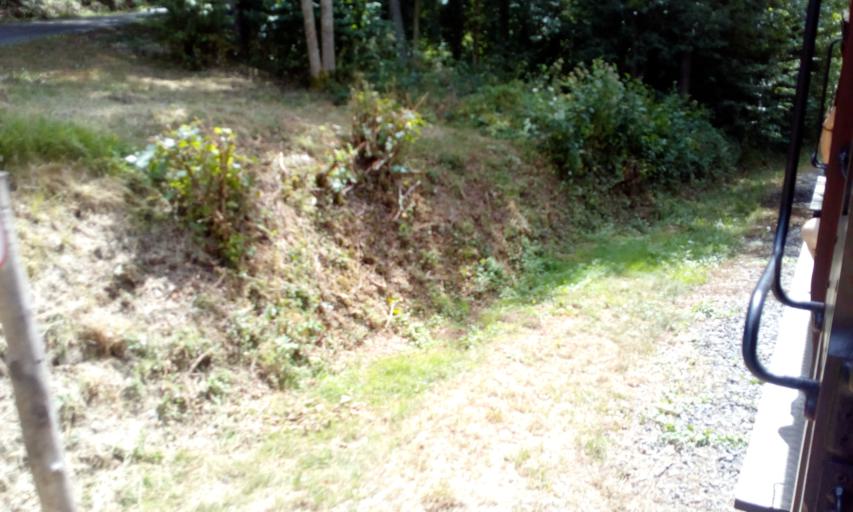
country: BE
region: Wallonia
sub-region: Province de Namur
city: Rochefort
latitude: 50.1247
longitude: 5.2018
